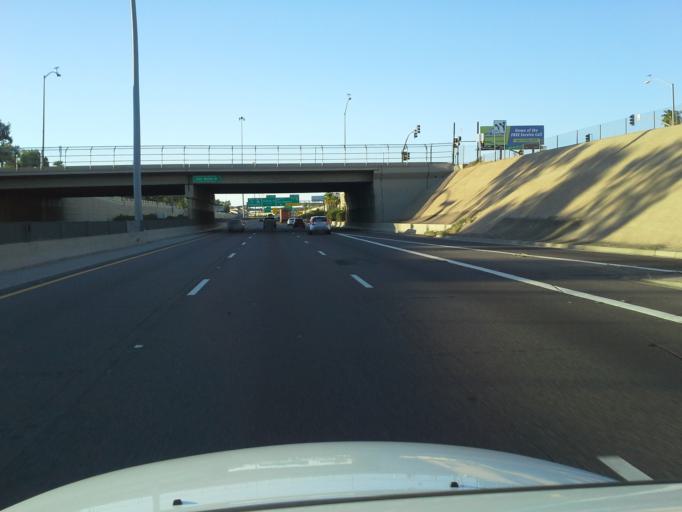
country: US
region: Arizona
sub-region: Maricopa County
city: Phoenix
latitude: 33.4503
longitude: -112.1081
